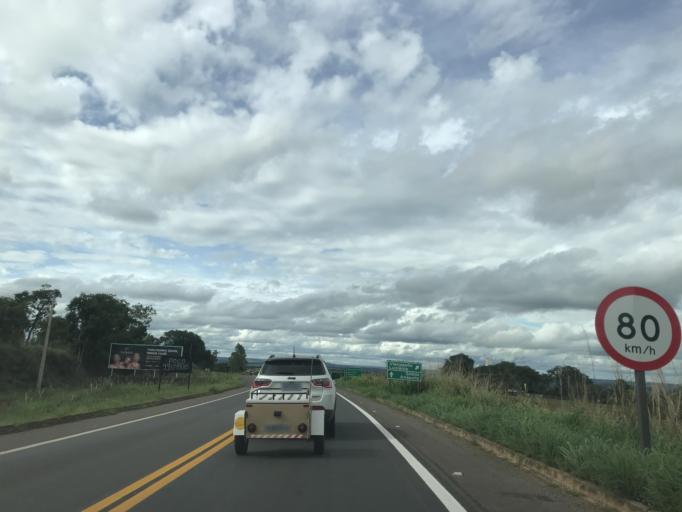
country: BR
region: Goias
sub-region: Piracanjuba
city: Piracanjuba
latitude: -17.2103
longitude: -48.7078
